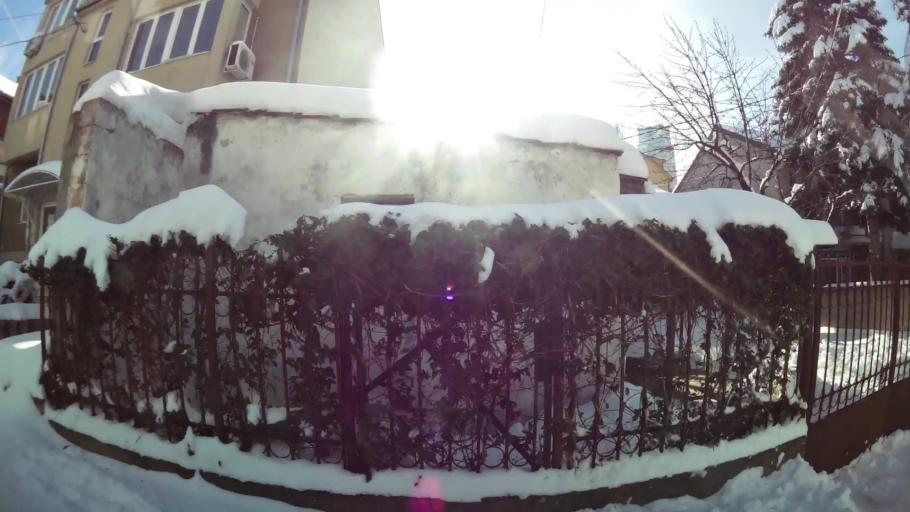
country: RS
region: Central Serbia
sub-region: Belgrade
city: Zvezdara
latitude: 44.7874
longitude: 20.5132
